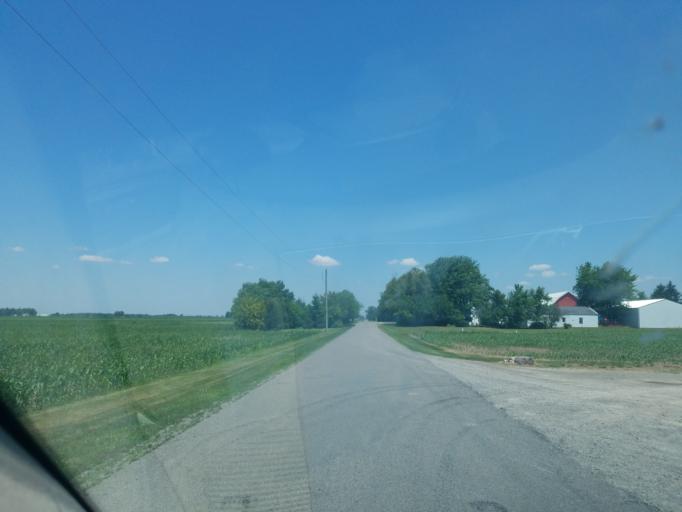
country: US
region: Ohio
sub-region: Allen County
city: Spencerville
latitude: 40.7623
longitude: -84.3494
